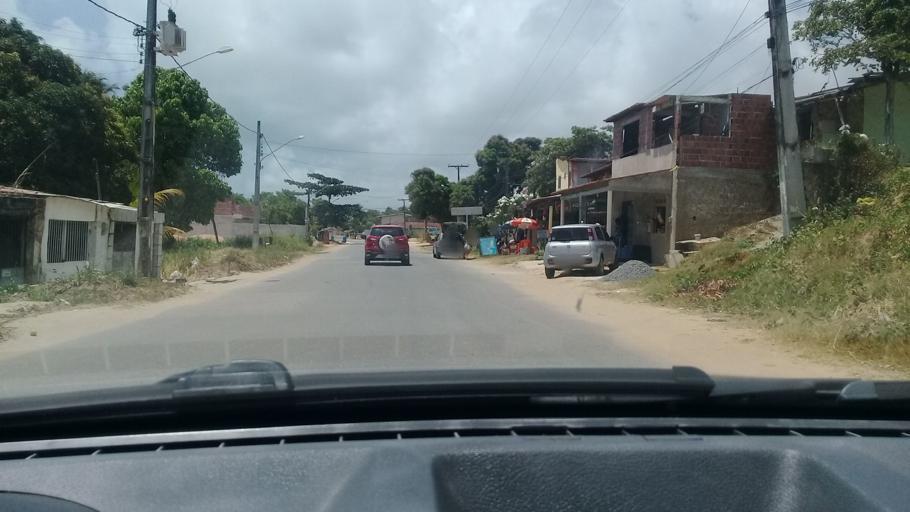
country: BR
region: Pernambuco
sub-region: Itamaraca
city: Itamaraca
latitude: -7.7940
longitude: -34.8418
